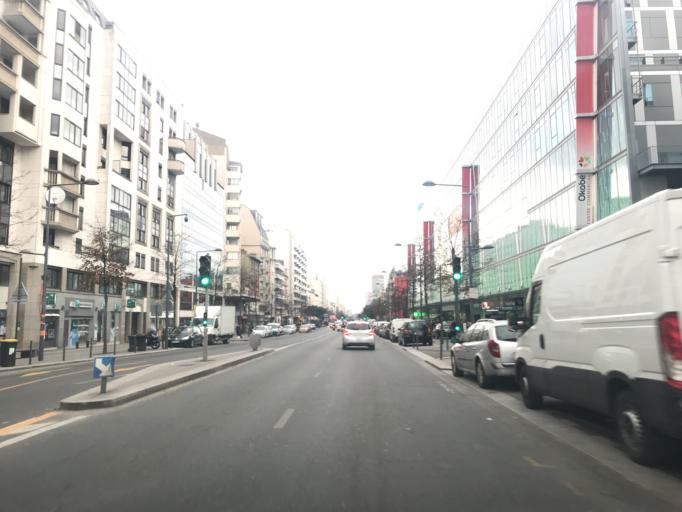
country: FR
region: Ile-de-France
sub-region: Departement du Val-de-Marne
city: Le Kremlin-Bicetre
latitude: 48.8105
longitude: 2.3622
